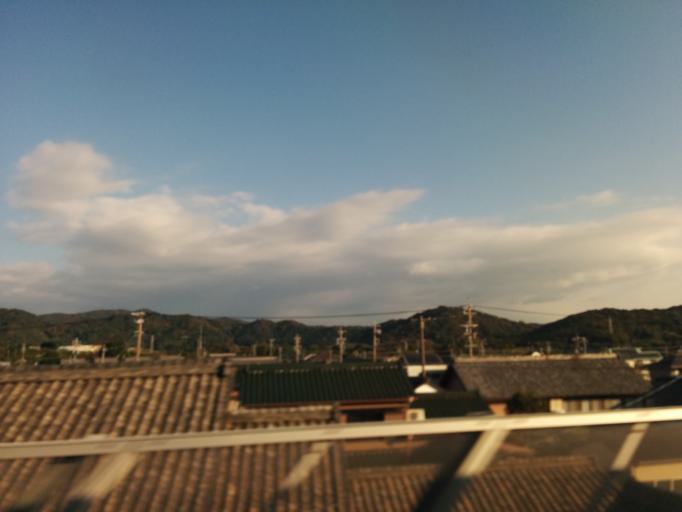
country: JP
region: Aichi
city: Gamagori
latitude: 34.8147
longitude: 137.2921
